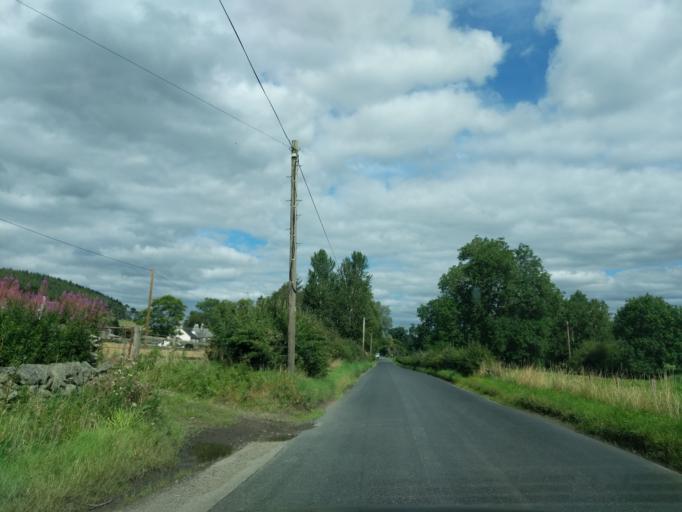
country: GB
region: Scotland
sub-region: The Scottish Borders
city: Peebles
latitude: 55.6236
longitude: -3.2997
